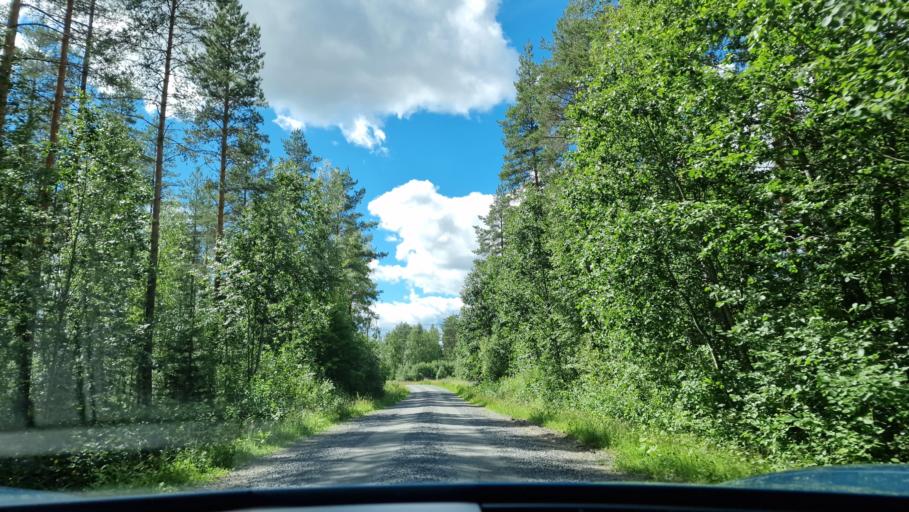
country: FI
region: Southern Ostrobothnia
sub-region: Jaerviseutu
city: Soini
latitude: 62.8479
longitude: 24.3383
